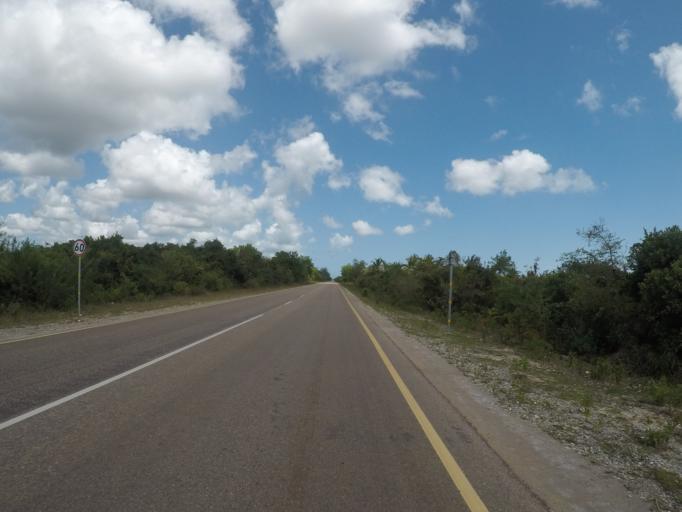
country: TZ
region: Zanzibar Central/South
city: Koani
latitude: -6.2502
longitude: 39.3549
